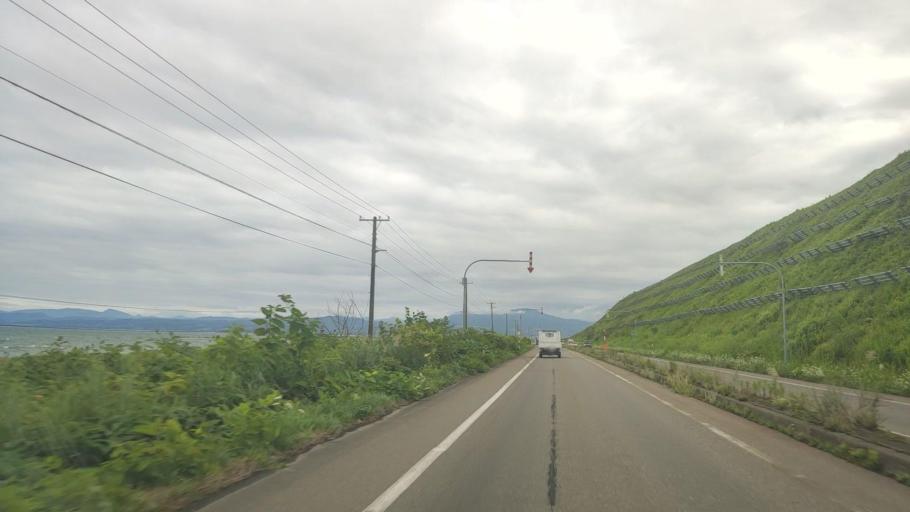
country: JP
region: Hokkaido
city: Niseko Town
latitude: 42.3290
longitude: 140.2774
